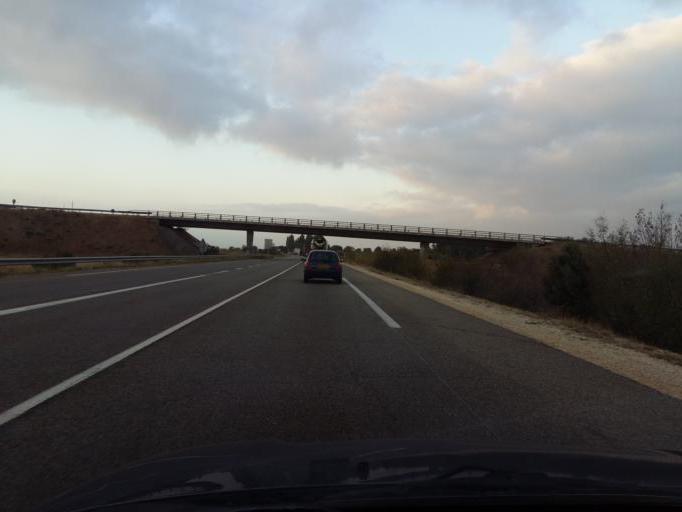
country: FR
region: Provence-Alpes-Cote d'Azur
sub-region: Departement des Bouches-du-Rhone
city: Istres
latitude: 43.5587
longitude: 4.9658
